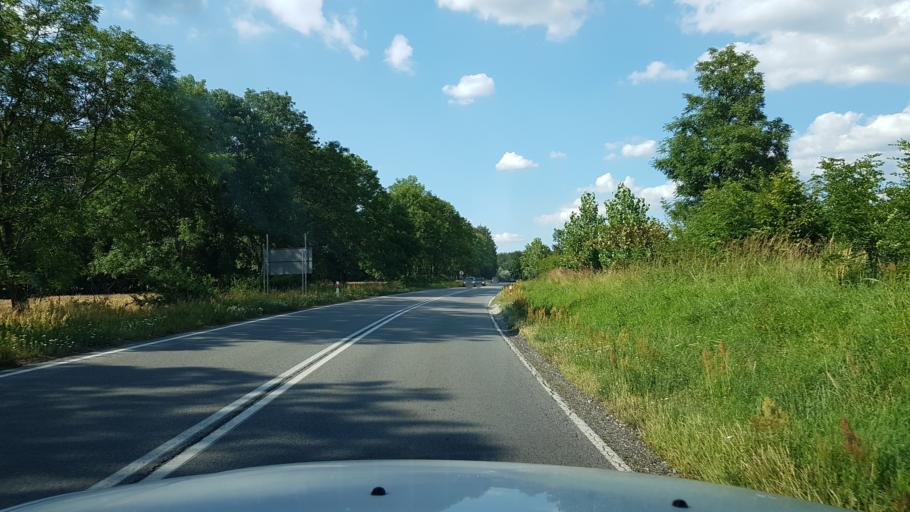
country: PL
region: West Pomeranian Voivodeship
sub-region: Powiat gryfinski
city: Stare Czarnowo
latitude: 53.3075
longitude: 14.7925
